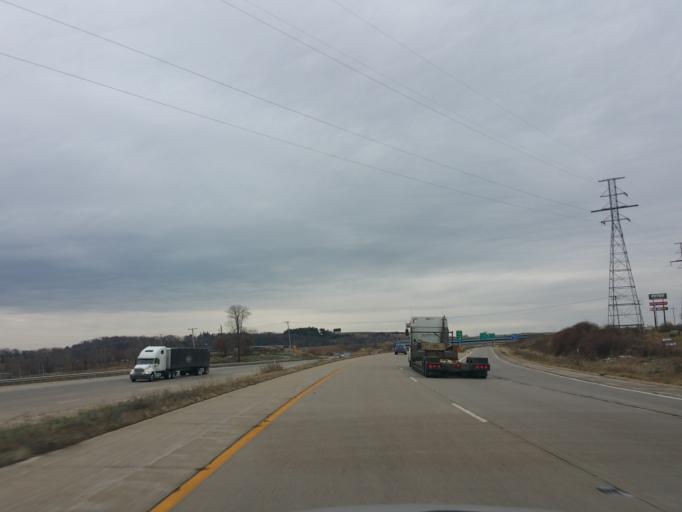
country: US
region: Wisconsin
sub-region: Columbia County
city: Portage
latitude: 43.4946
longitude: -89.4967
